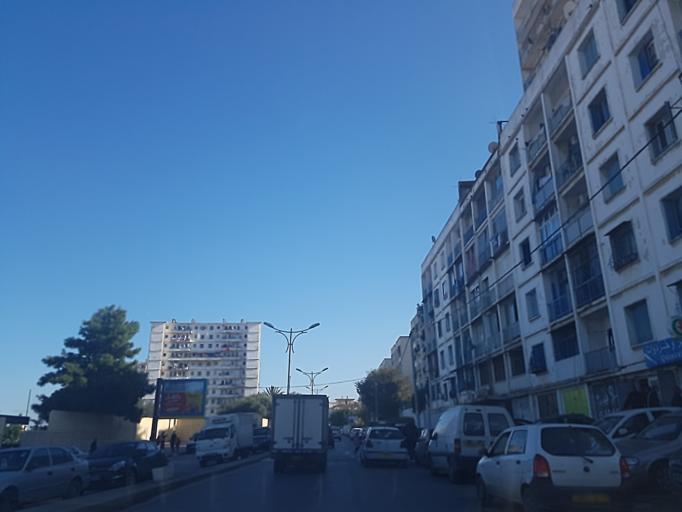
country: DZ
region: Alger
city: Birkhadem
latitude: 36.7349
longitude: 3.0979
